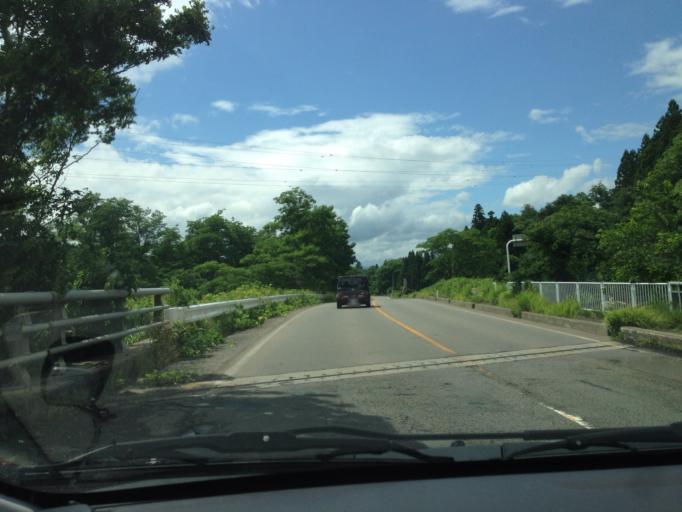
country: JP
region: Fukushima
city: Kitakata
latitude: 37.5792
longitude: 139.9247
